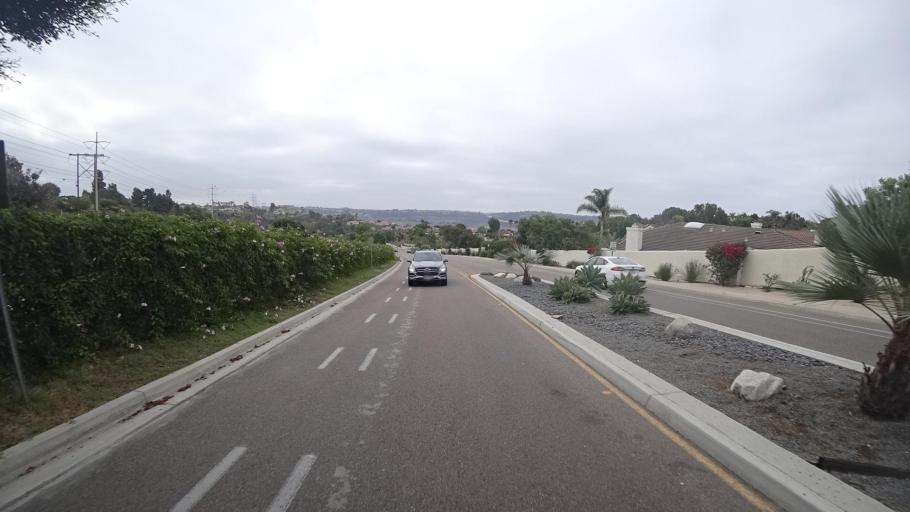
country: US
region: California
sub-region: San Diego County
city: Solana Beach
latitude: 32.9901
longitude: -117.2473
